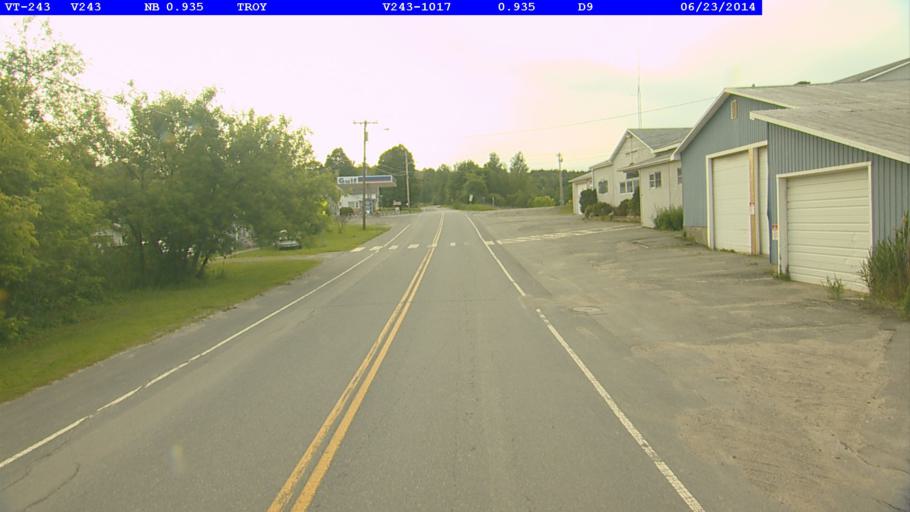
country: US
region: Vermont
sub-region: Orleans County
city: Newport
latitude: 44.9972
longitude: -72.4049
